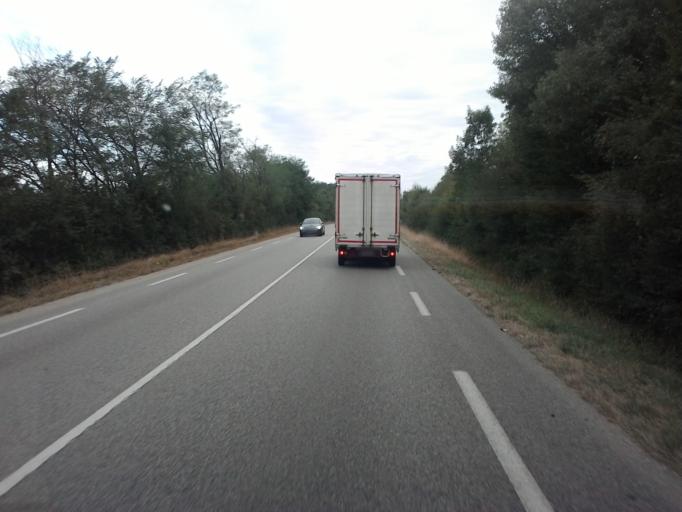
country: FR
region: Rhone-Alpes
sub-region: Departement de l'Ain
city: Ambronay
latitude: 46.0162
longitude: 5.3400
